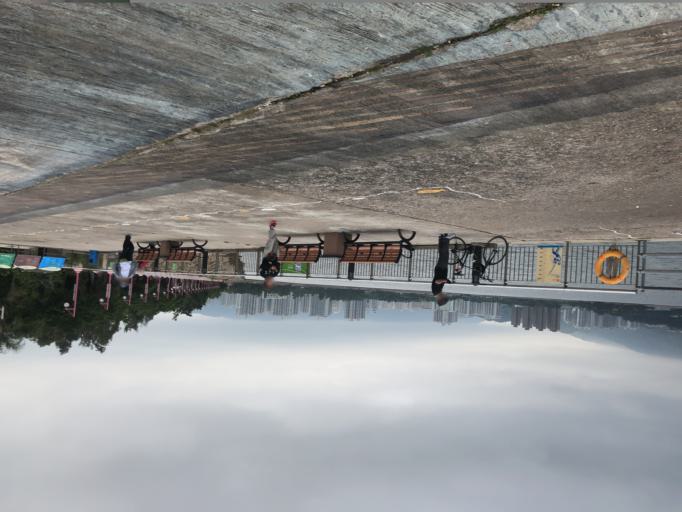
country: HK
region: Tai Po
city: Tai Po
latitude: 22.4509
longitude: 114.1931
